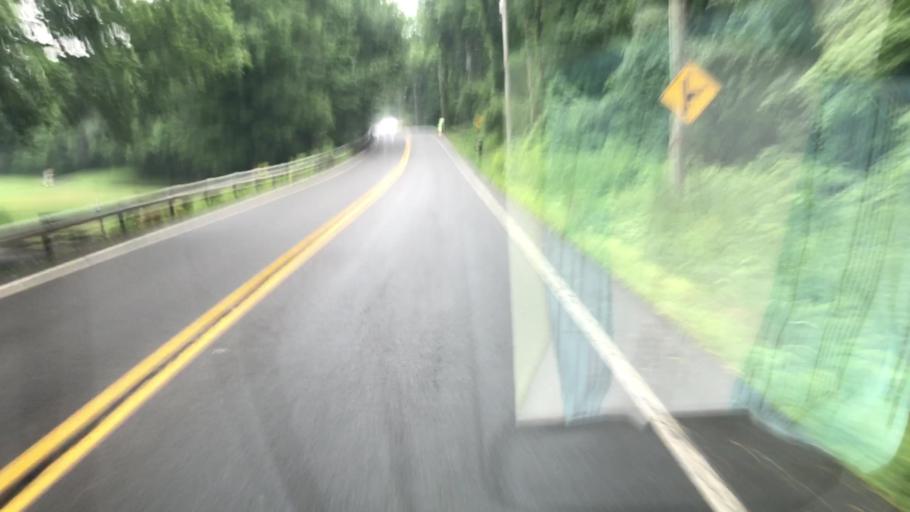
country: US
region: New York
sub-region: Onondaga County
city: Manlius
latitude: 43.0008
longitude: -75.9971
